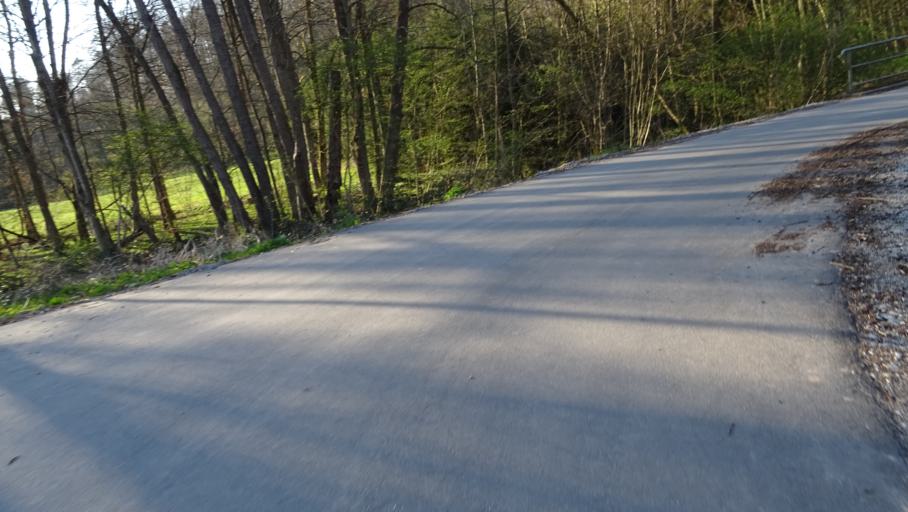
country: DE
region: Baden-Wuerttemberg
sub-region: Karlsruhe Region
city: Limbach
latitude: 49.4019
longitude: 9.2076
